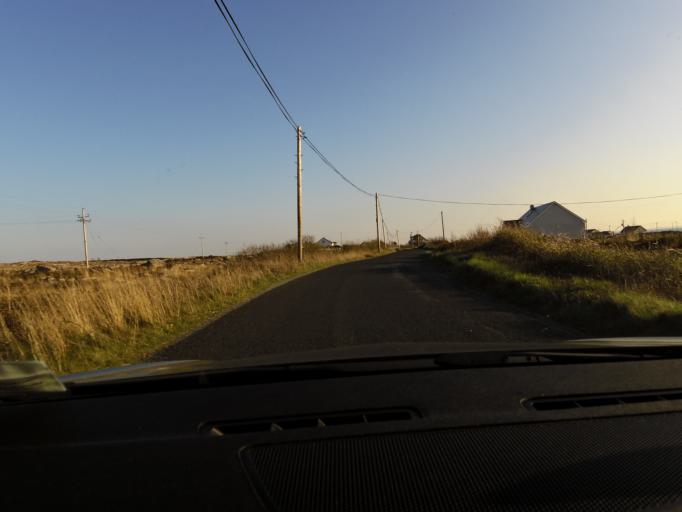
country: IE
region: Connaught
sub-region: County Galway
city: Oughterard
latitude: 53.2558
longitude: -9.5424
